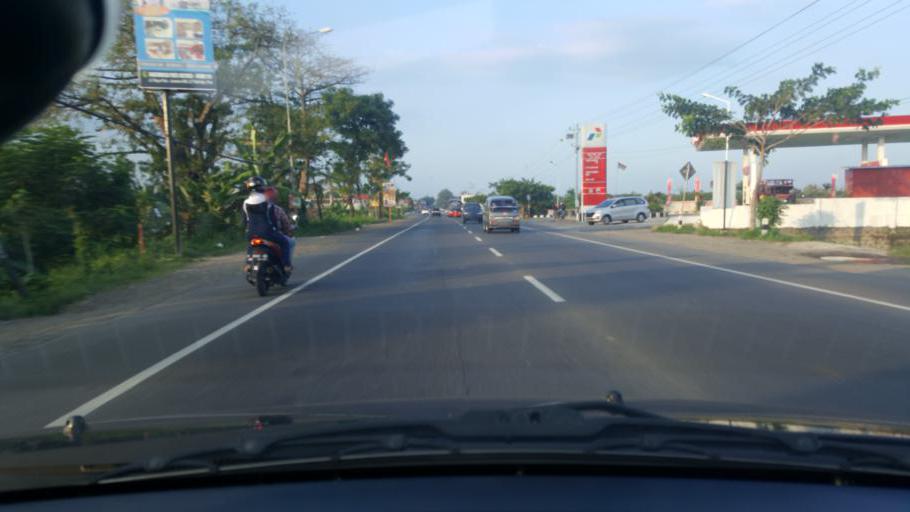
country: ID
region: Central Java
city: Gemiring
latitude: -6.7810
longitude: 110.9894
